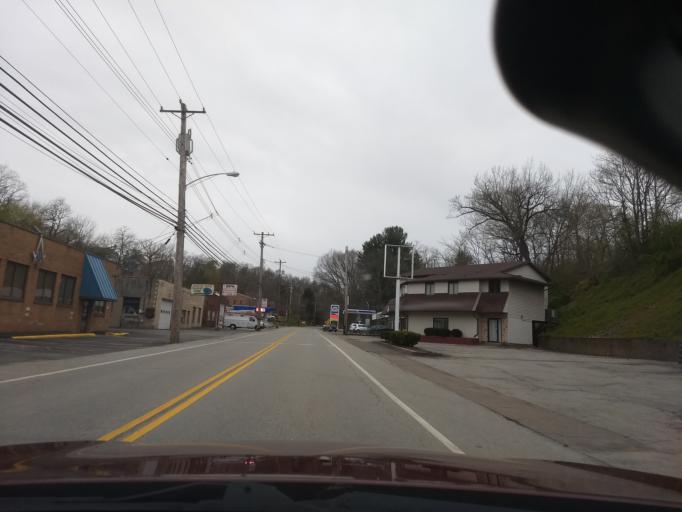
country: US
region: Pennsylvania
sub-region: Allegheny County
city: Dormont
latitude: 40.3834
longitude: -80.0191
